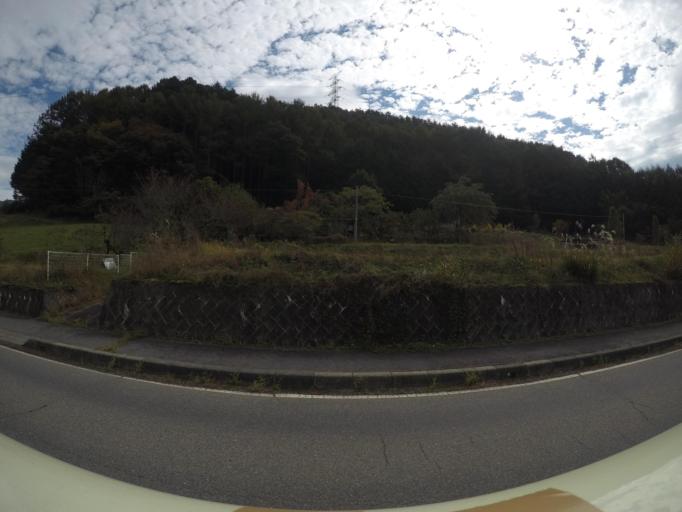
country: JP
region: Nagano
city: Ina
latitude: 35.8544
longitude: 138.0777
